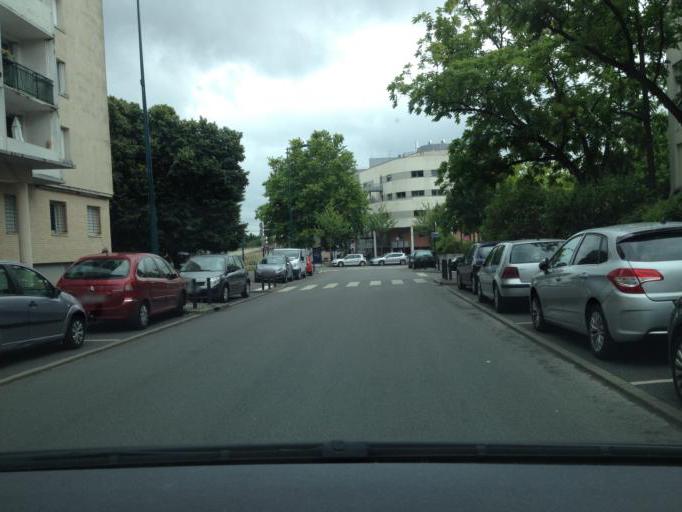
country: FR
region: Ile-de-France
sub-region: Departement de l'Essonne
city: Massy
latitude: 48.7322
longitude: 2.2911
